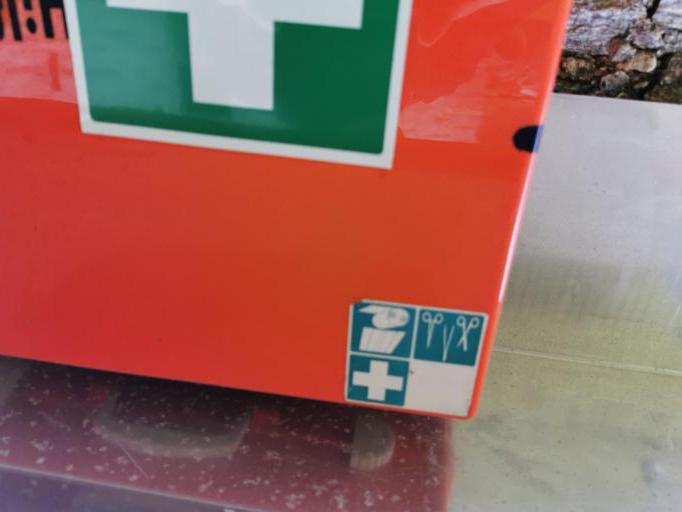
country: CH
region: Ticino
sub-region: Leventina District
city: Bodio
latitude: 46.3761
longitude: 8.8926
